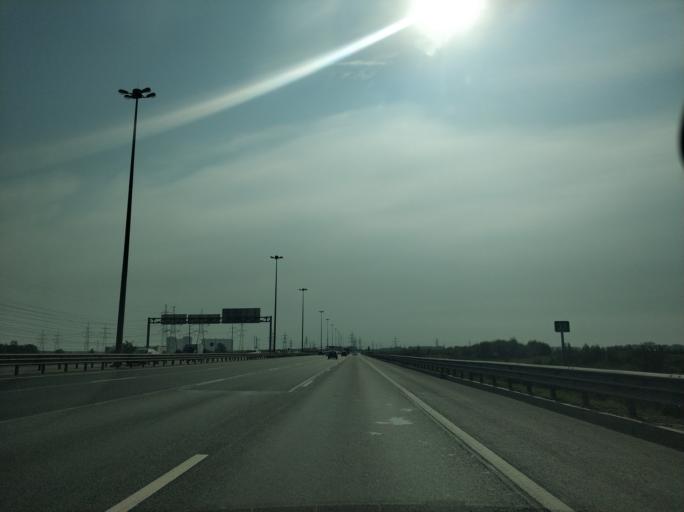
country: RU
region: Leningrad
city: Murino
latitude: 60.0266
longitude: 30.4487
